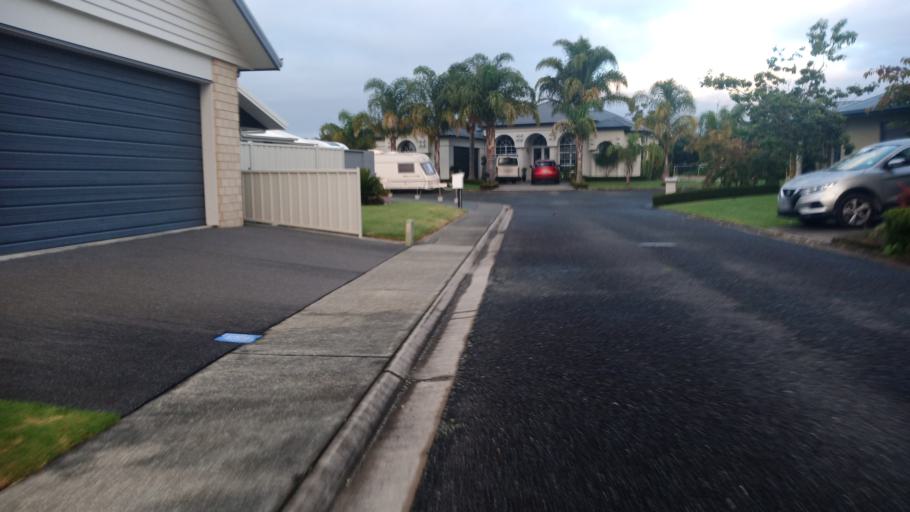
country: NZ
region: Gisborne
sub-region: Gisborne District
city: Gisborne
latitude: -38.6396
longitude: 177.9966
